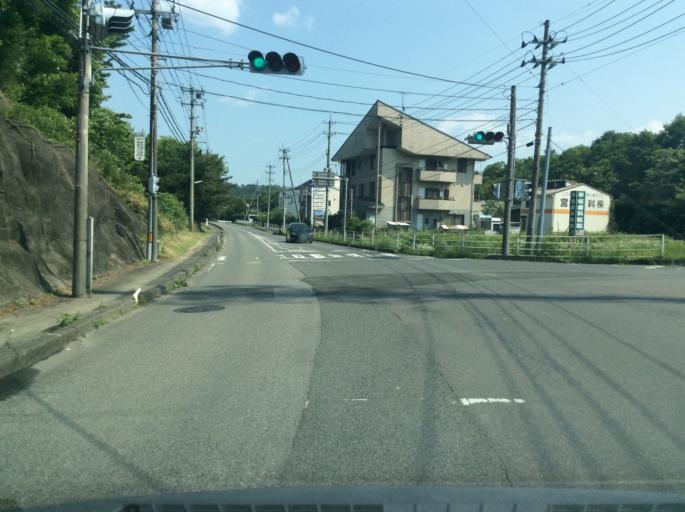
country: JP
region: Fukushima
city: Ishikawa
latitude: 37.1052
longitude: 140.2305
